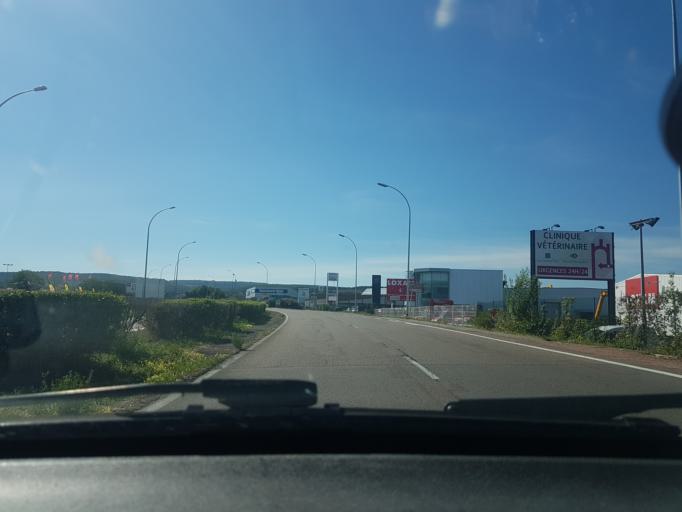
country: FR
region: Bourgogne
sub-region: Departement de la Cote-d'Or
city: Chenove
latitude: 47.2819
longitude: 5.0147
